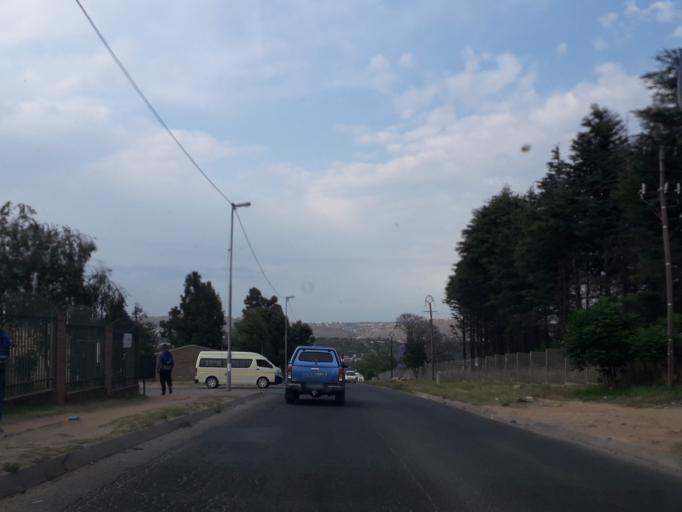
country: ZA
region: Gauteng
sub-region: West Rand District Municipality
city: Muldersdriseloop
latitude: -26.0747
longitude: 27.9117
